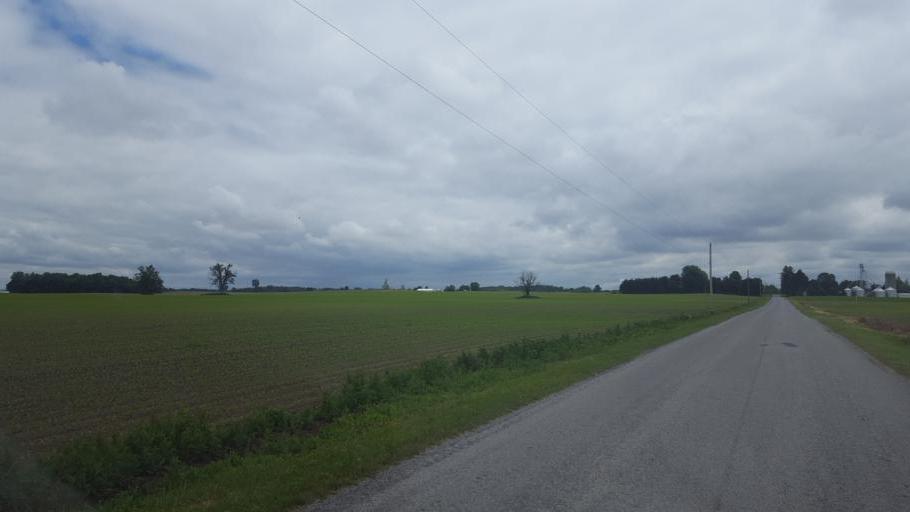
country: US
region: Ohio
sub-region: Crawford County
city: Bucyrus
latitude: 40.7753
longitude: -83.0867
